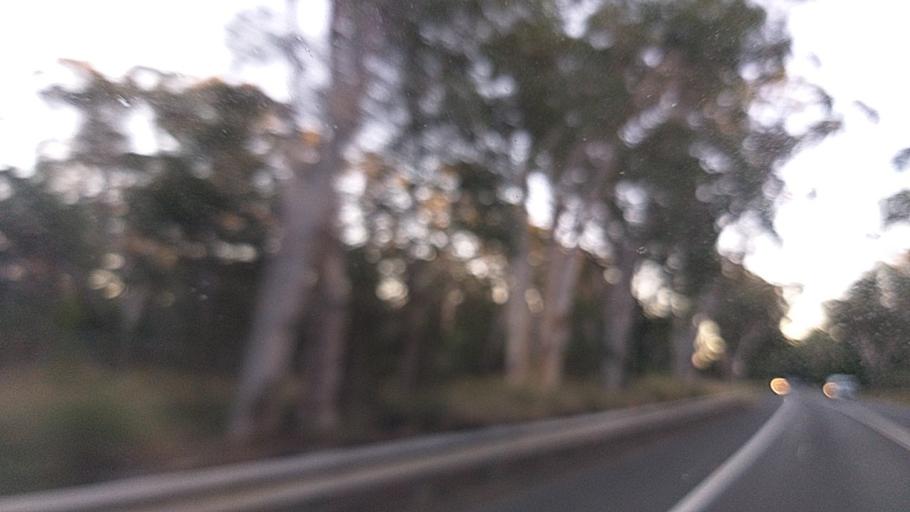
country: AU
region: New South Wales
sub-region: Hawkesbury
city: South Windsor
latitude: -33.6501
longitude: 150.7920
